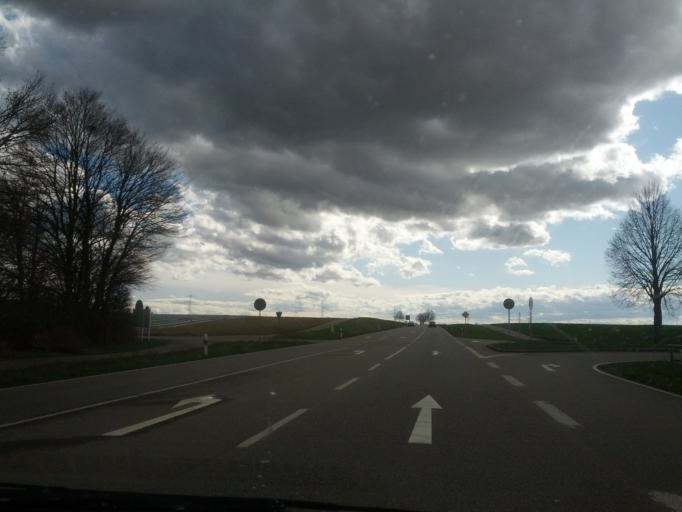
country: DE
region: Baden-Wuerttemberg
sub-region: Freiburg Region
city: Eschbach
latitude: 47.8981
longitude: 7.6771
